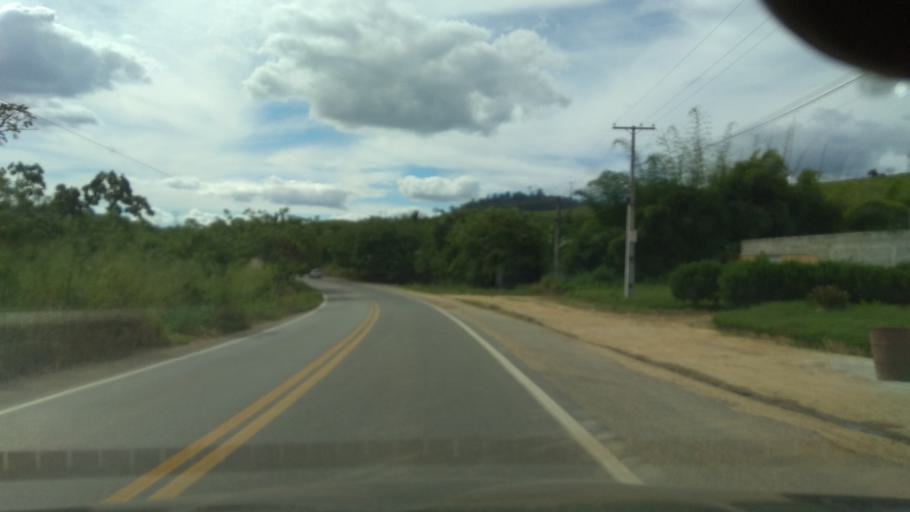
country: BR
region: Bahia
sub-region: Ipiau
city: Ipiau
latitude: -14.1115
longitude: -39.7733
